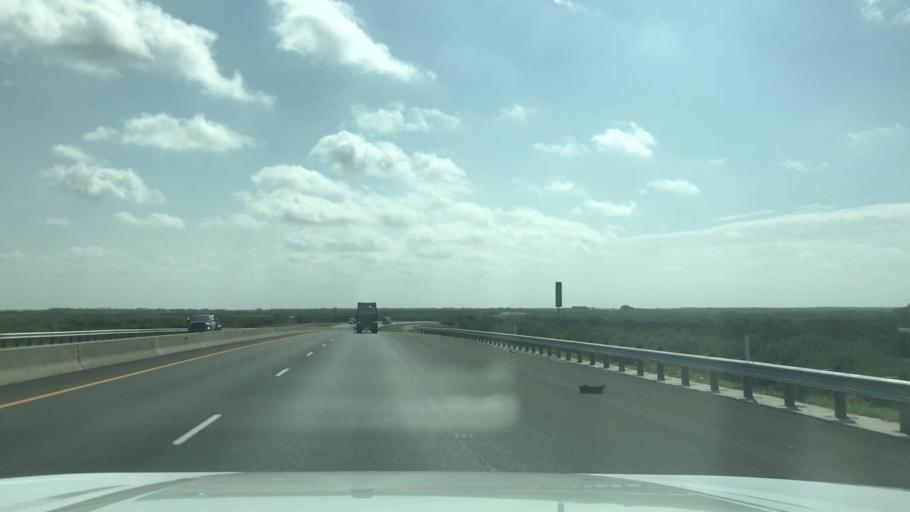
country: US
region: Texas
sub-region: Nolan County
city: Sweetwater
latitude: 32.4900
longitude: -100.2299
